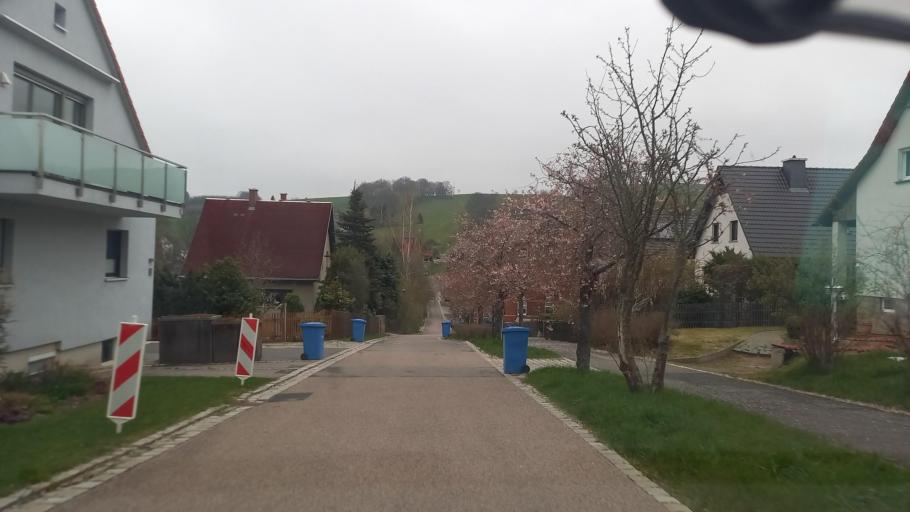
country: DE
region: Saxony
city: Reinsdorf
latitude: 50.7003
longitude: 12.5485
